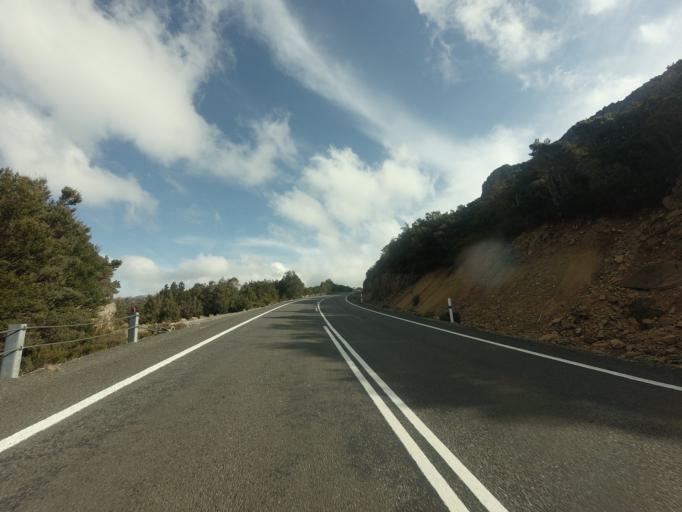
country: AU
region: Tasmania
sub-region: Meander Valley
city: Deloraine
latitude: -41.7292
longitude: 146.7208
